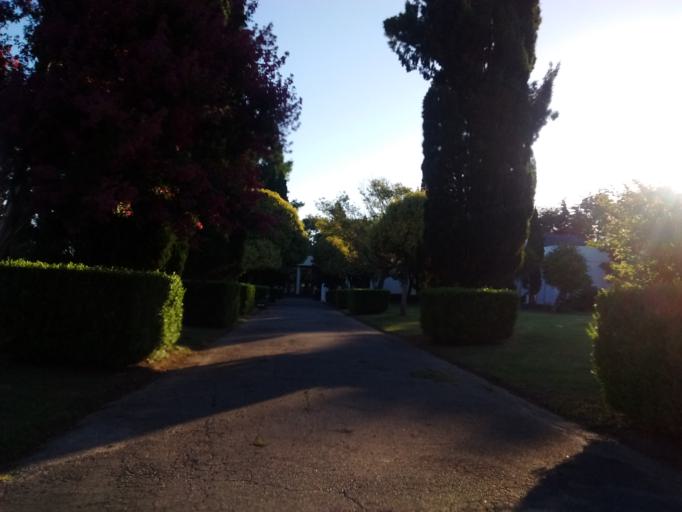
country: AR
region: Santa Fe
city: Funes
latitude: -32.9189
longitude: -60.7911
